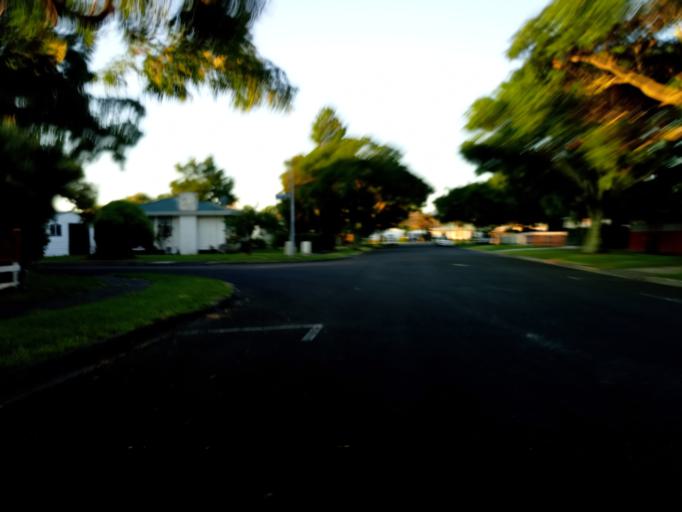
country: NZ
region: Gisborne
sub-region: Gisborne District
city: Gisborne
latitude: -38.6437
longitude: 178.0041
